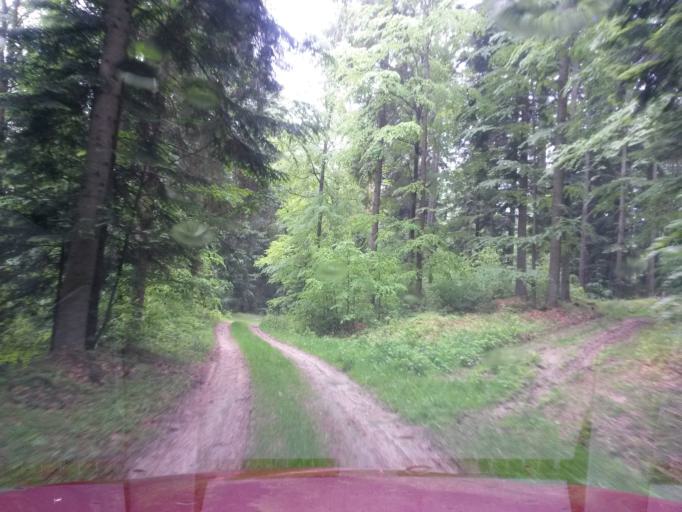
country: SK
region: Kosicky
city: Medzev
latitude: 48.7855
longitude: 20.7868
